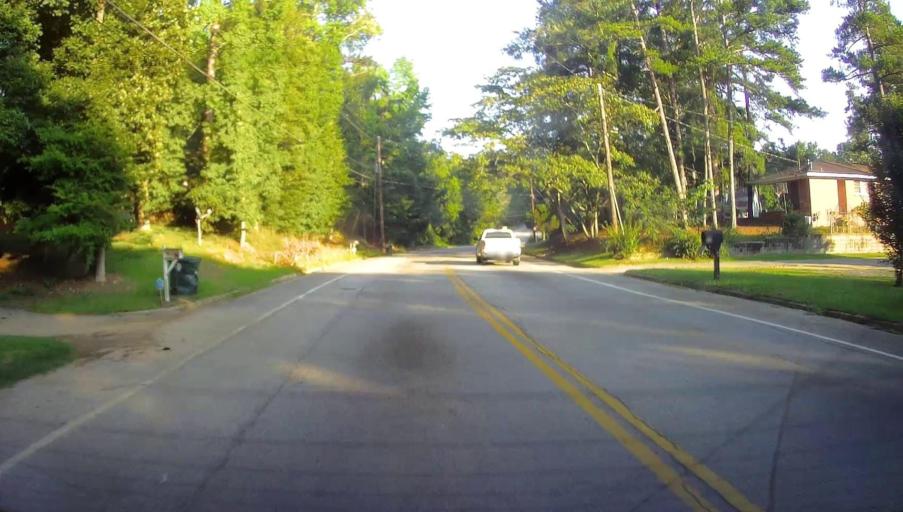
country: US
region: Georgia
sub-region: Bibb County
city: Macon
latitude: 32.8635
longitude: -83.6967
